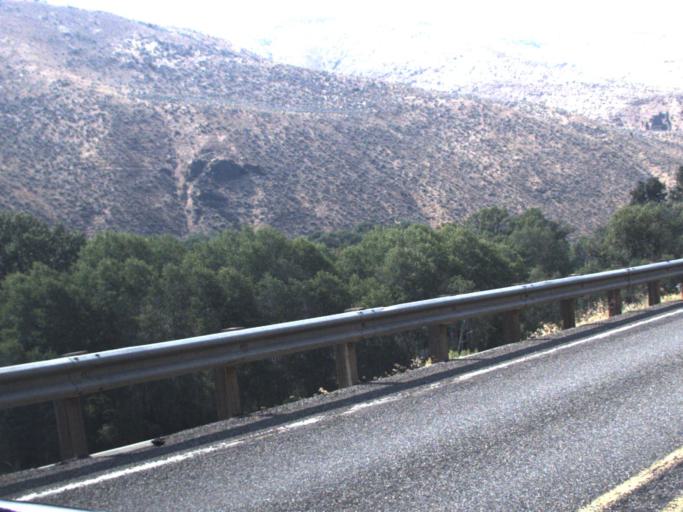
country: US
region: Washington
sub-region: Kittitas County
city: Ellensburg
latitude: 46.9085
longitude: -120.5025
